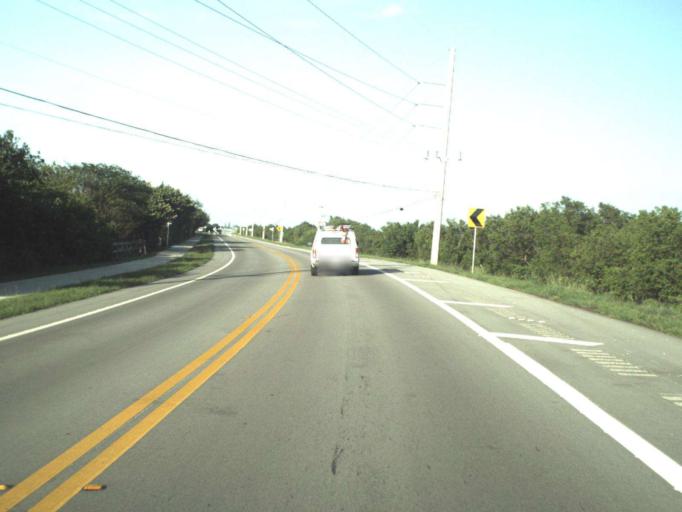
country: US
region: Florida
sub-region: Monroe County
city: Islamorada
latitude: 24.8364
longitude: -80.7622
